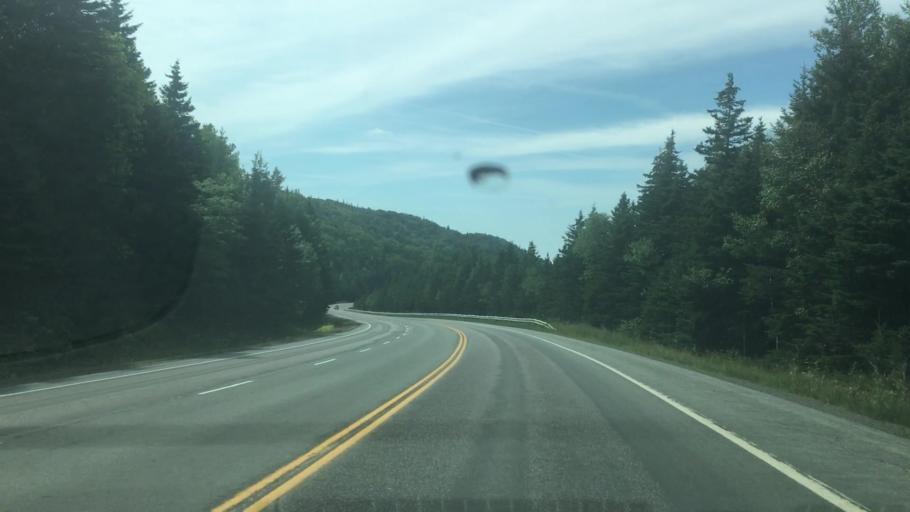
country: CA
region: Nova Scotia
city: Sydney Mines
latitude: 46.2437
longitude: -60.5590
